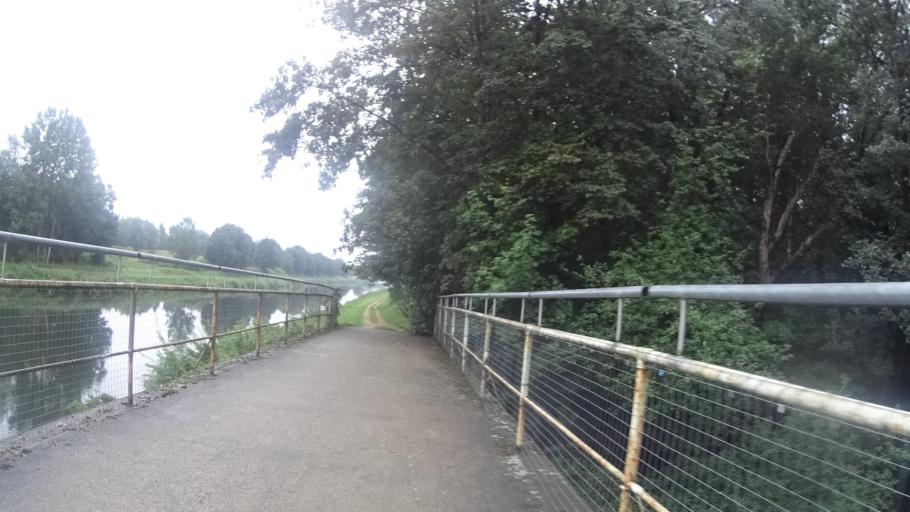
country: DE
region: Schleswig-Holstein
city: Guster
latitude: 53.5462
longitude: 10.6825
